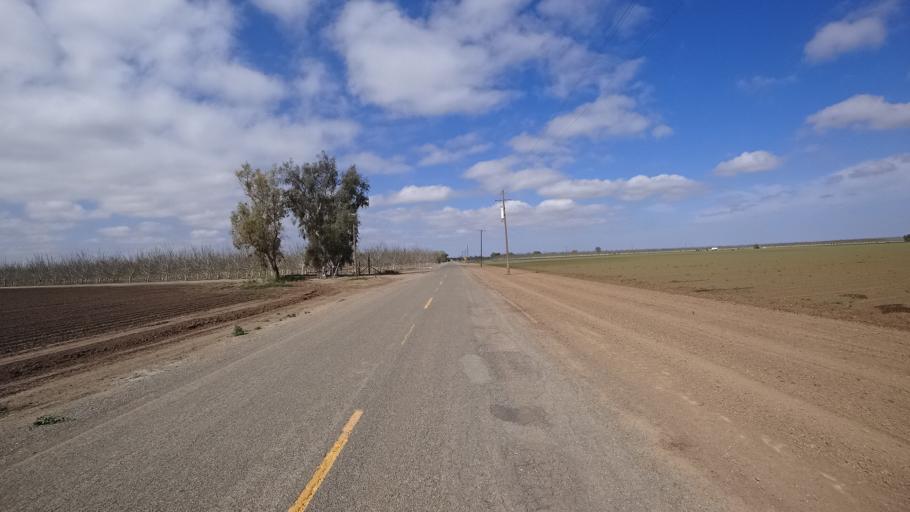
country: US
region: California
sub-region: Colusa County
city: Colusa
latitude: 39.4201
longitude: -121.9379
